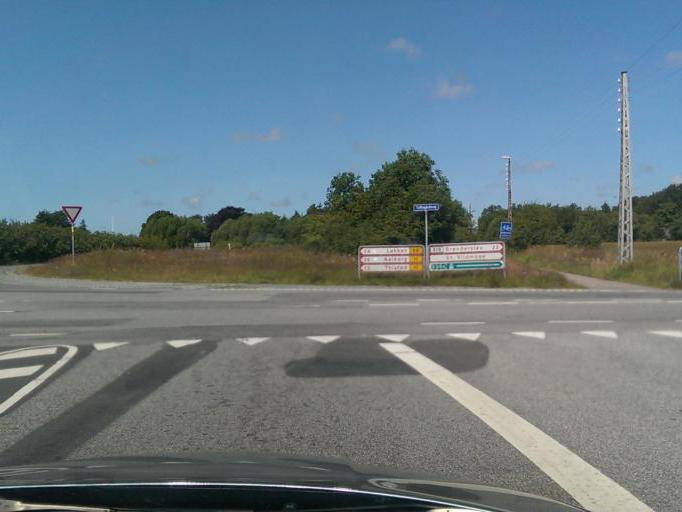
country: DK
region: North Denmark
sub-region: Jammerbugt Kommune
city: Abybro
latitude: 57.1664
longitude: 9.7226
